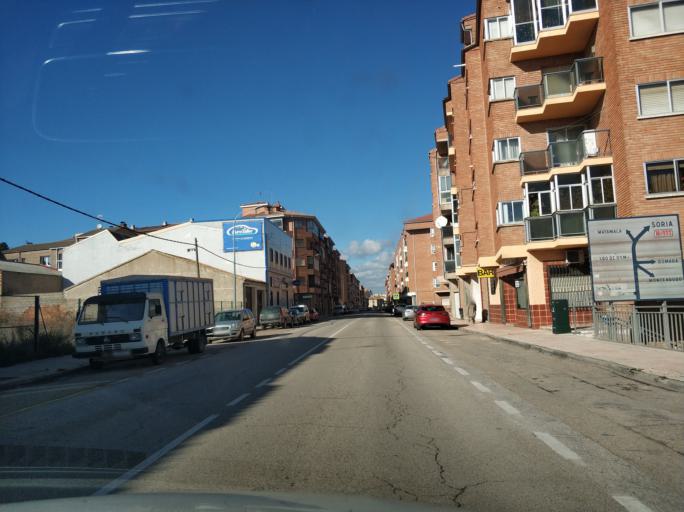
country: ES
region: Castille and Leon
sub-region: Provincia de Soria
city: Almazan
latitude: 41.4822
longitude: -2.5292
